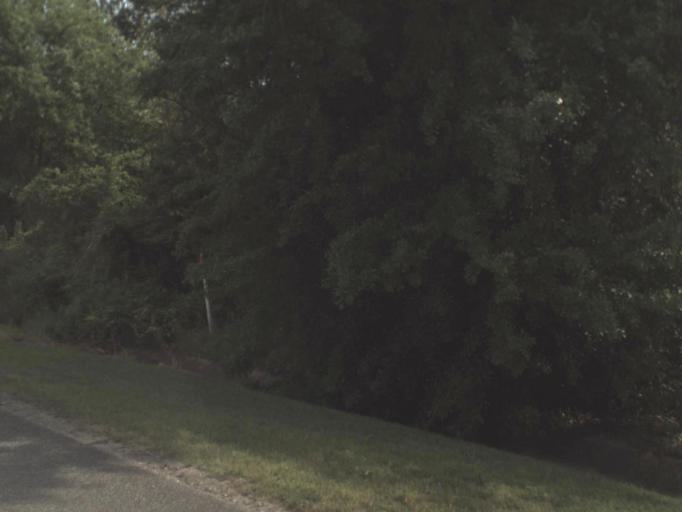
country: US
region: Florida
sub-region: Escambia County
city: Gonzalez
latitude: 30.5574
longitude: -87.2853
